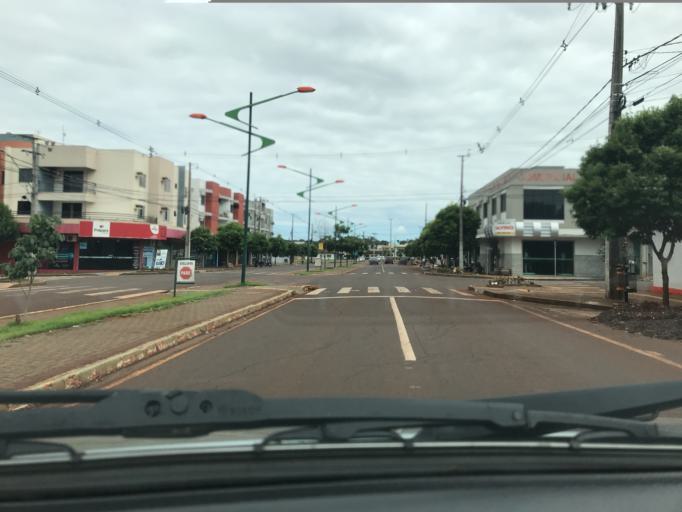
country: BR
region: Parana
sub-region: Palotina
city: Palotina
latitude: -24.2794
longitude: -53.8412
